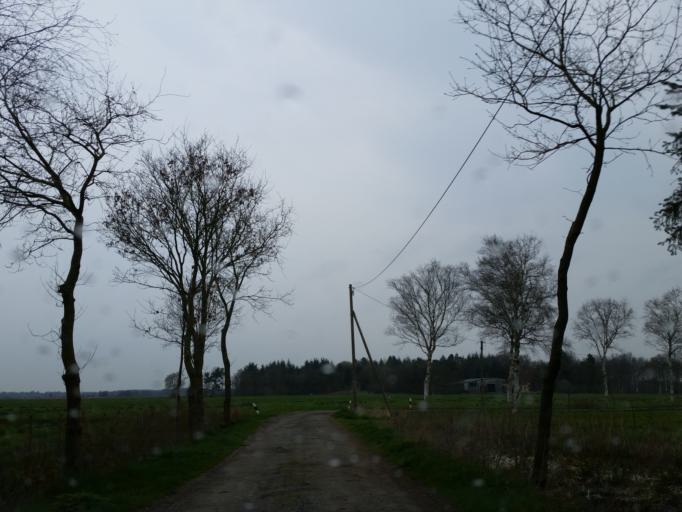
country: DE
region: Lower Saxony
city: Armstorf
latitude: 53.5884
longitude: 9.0070
